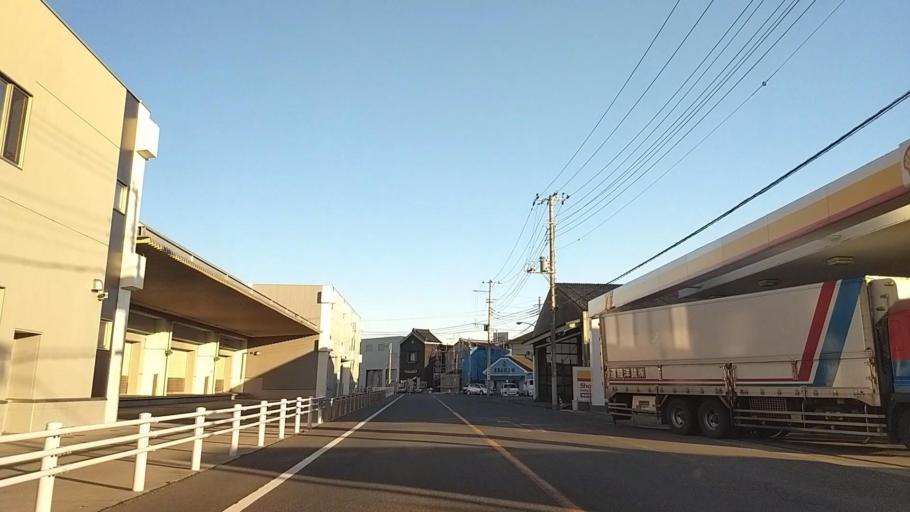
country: JP
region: Chiba
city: Hasaki
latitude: 35.7337
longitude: 140.8395
